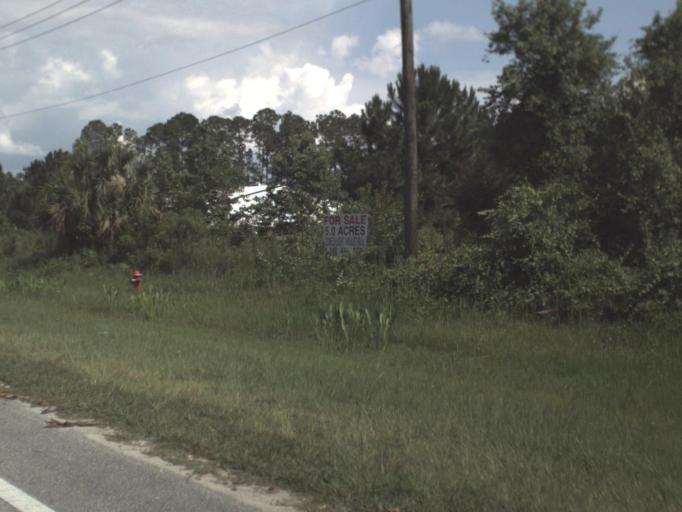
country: US
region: Florida
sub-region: Putnam County
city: Palatka
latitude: 29.6627
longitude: -81.6823
